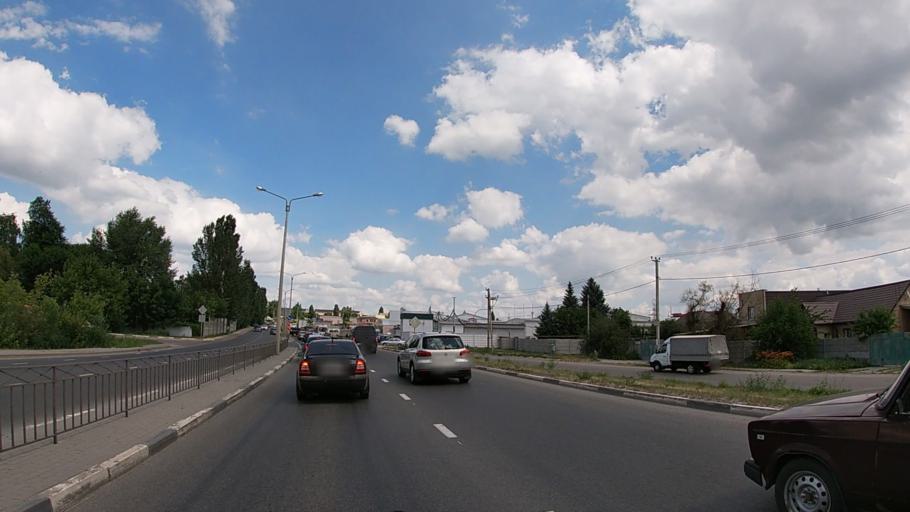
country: RU
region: Belgorod
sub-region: Belgorodskiy Rayon
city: Belgorod
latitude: 50.6094
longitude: 36.5338
